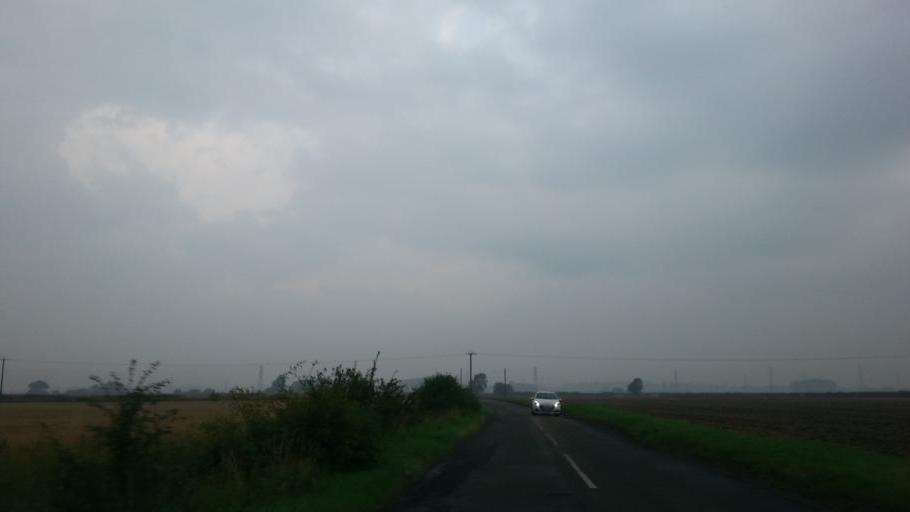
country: GB
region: England
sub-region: Nottinghamshire
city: Farndon
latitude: 53.0075
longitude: -0.8417
